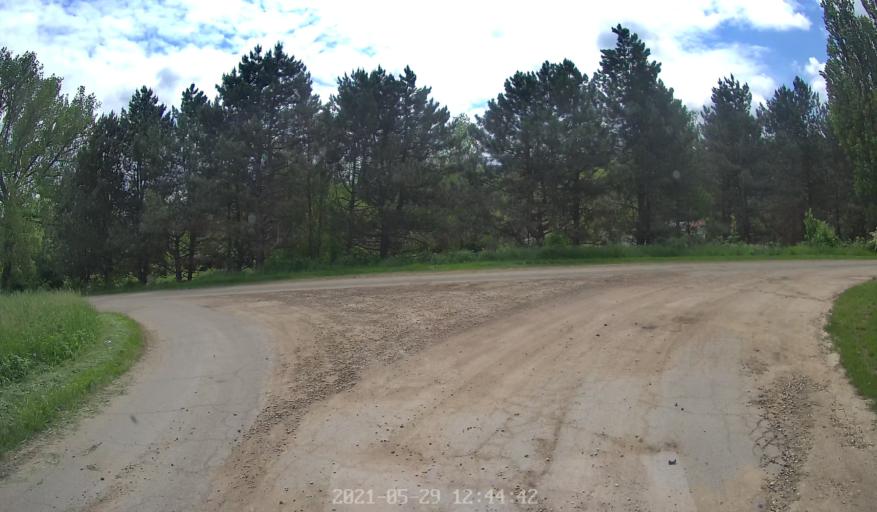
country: MD
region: Hincesti
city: Hincesti
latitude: 46.8694
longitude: 28.6406
